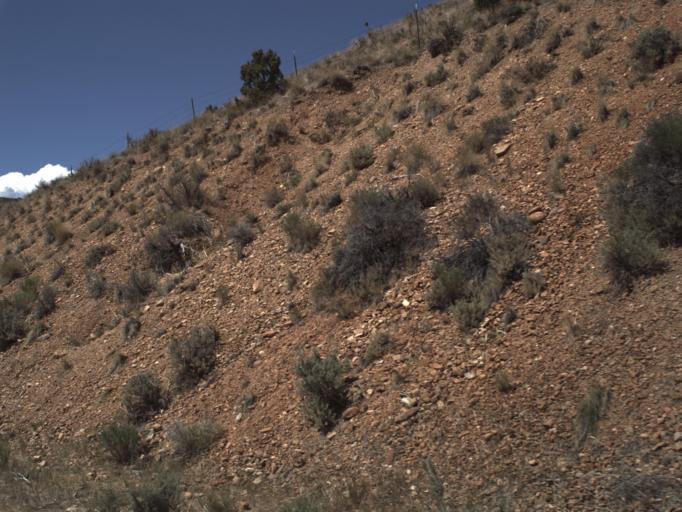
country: US
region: Utah
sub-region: Rich County
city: Randolph
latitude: 41.4994
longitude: -111.2758
